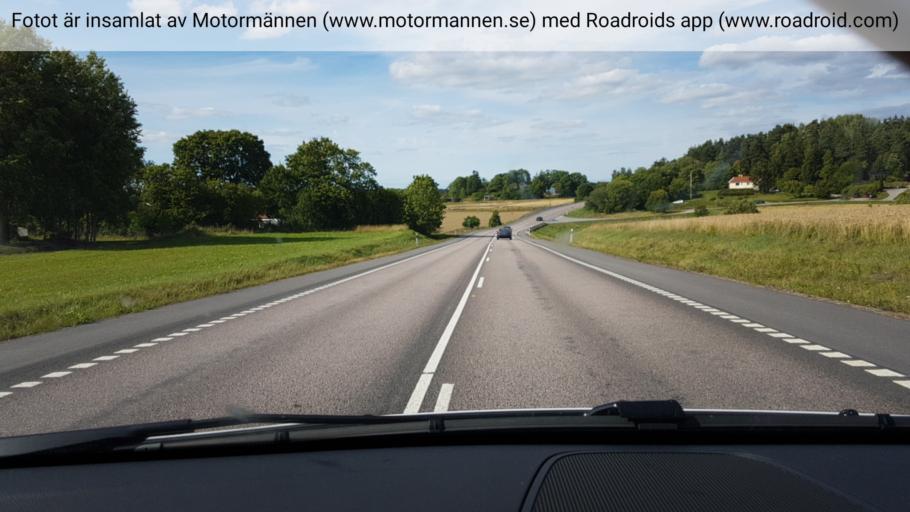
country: SE
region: Soedermanland
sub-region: Trosa Kommun
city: Vagnharad
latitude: 59.0160
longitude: 17.5926
